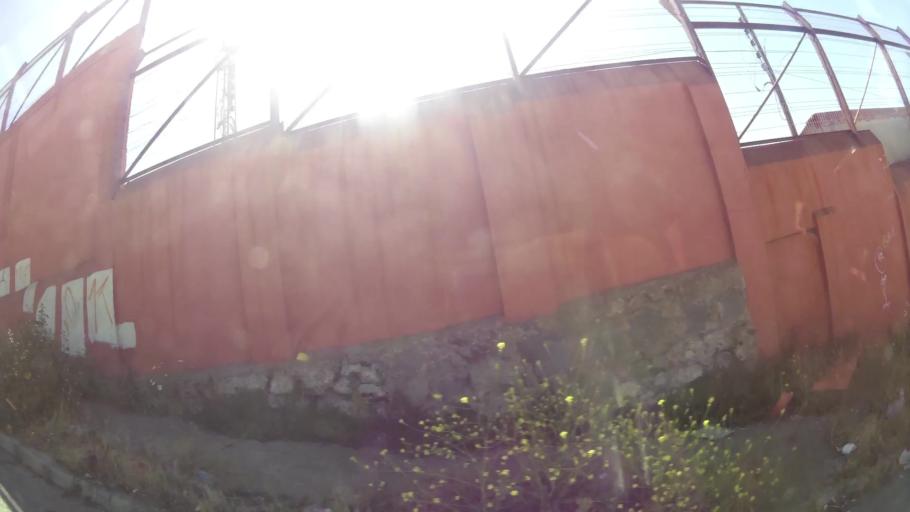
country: CL
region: Valparaiso
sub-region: Provincia de Valparaiso
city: Valparaiso
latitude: -33.0275
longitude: -71.6411
